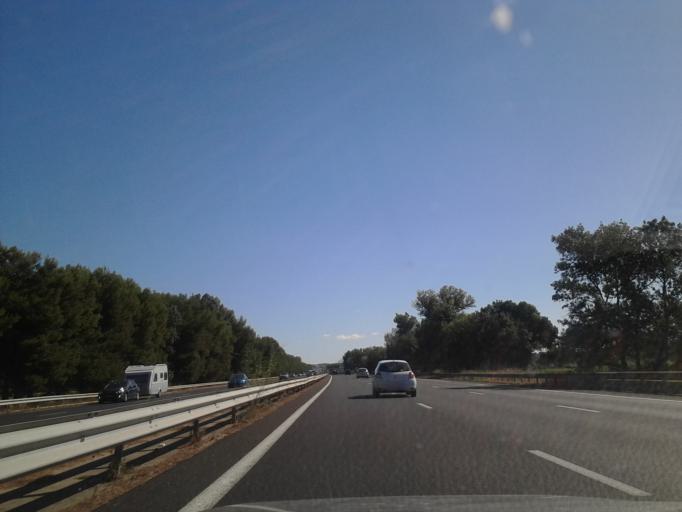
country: FR
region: Languedoc-Roussillon
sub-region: Departement de l'Herault
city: Sauvian
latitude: 43.3140
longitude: 3.2565
